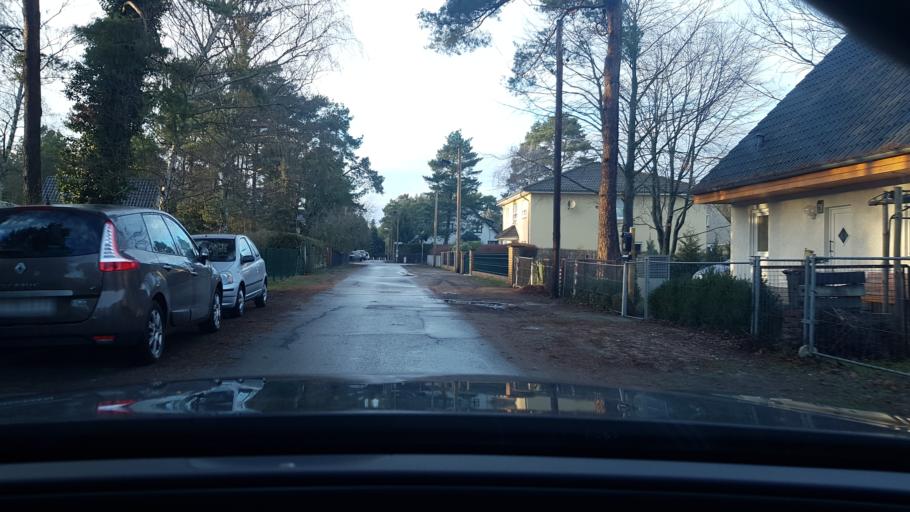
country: DE
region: Berlin
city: Muggelheim
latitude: 52.4195
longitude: 13.6692
